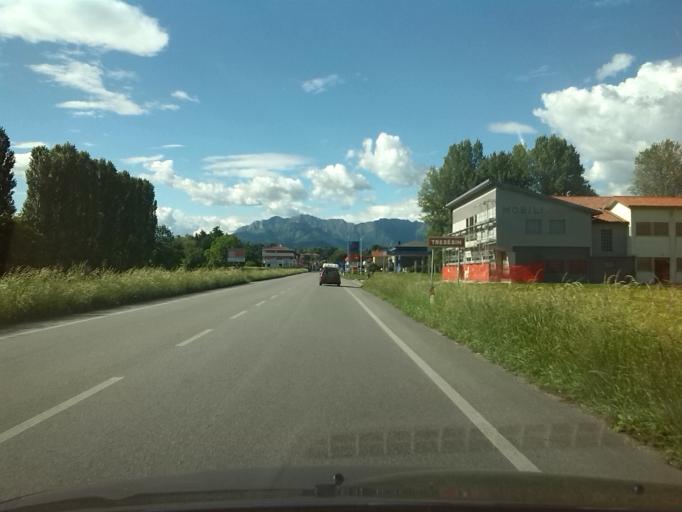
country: IT
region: Friuli Venezia Giulia
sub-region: Provincia di Udine
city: Reana del Roiale
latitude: 46.1487
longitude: 13.2200
